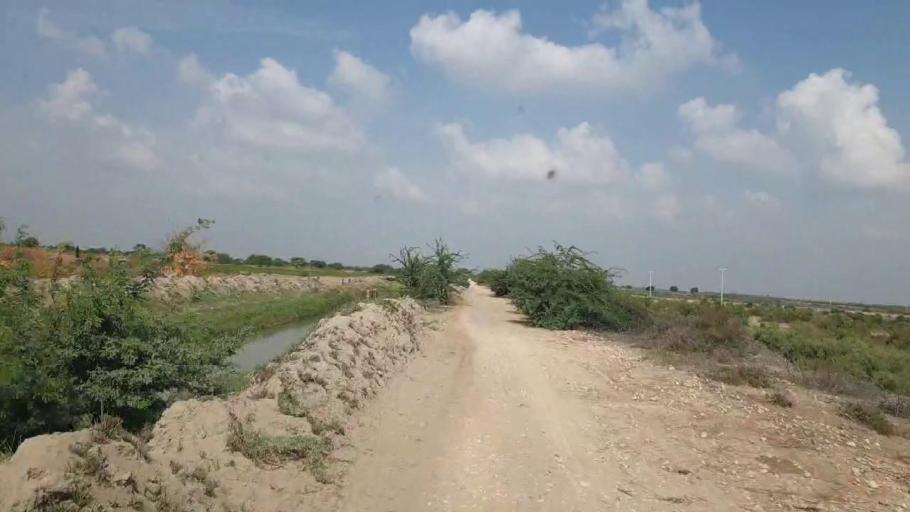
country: PK
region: Sindh
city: Badin
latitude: 24.5000
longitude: 68.6557
